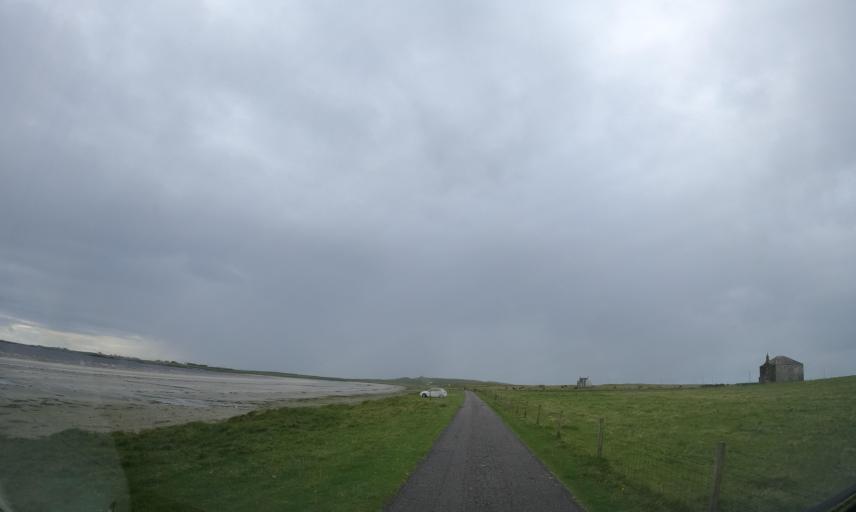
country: GB
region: Scotland
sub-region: Eilean Siar
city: Barra
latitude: 56.5200
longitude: -6.8105
